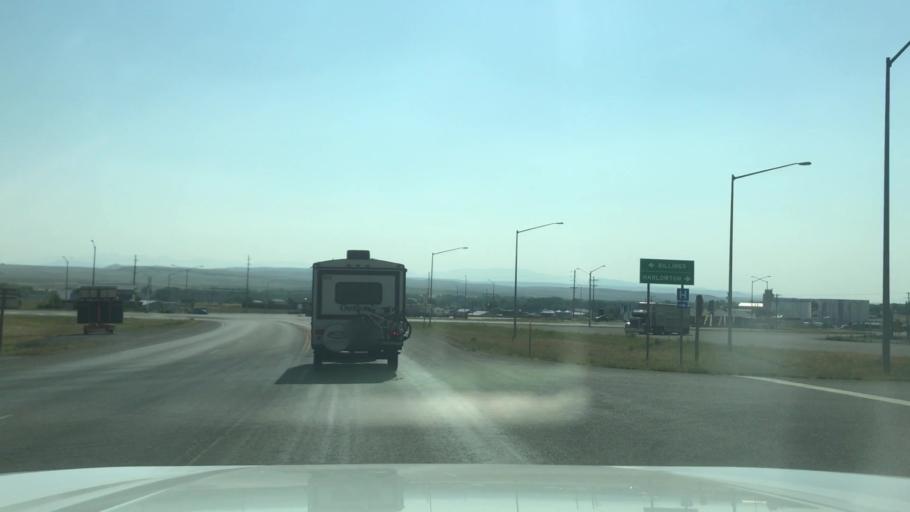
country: US
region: Montana
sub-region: Wheatland County
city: Harlowton
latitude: 46.4375
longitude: -109.8117
